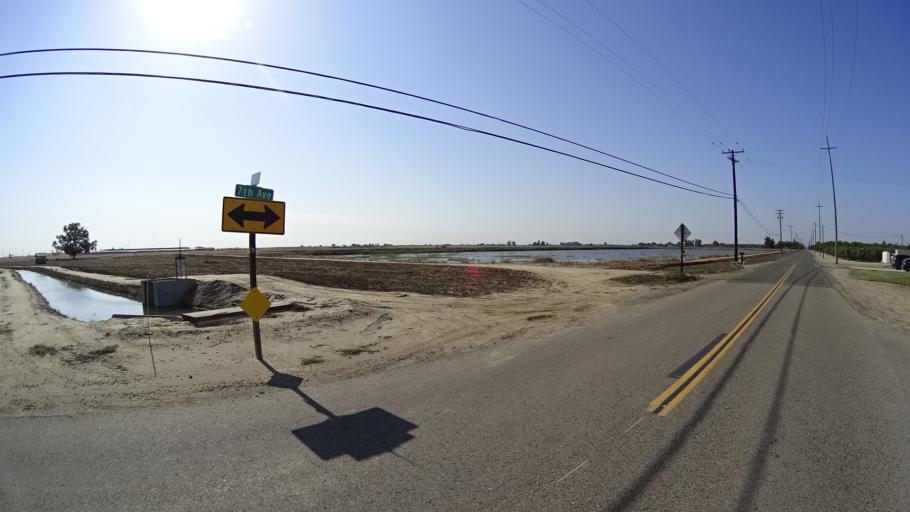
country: US
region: California
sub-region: Kings County
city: Home Garden
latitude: 36.3265
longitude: -119.5831
